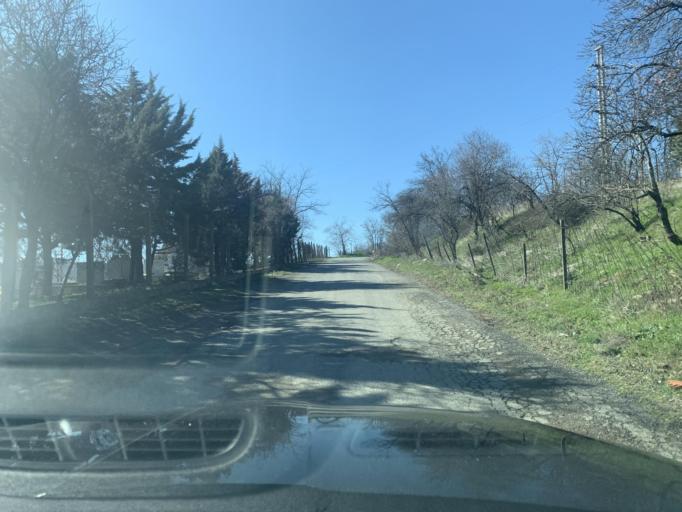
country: MK
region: Demir Kapija
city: Demir Kapija
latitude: 41.4092
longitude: 22.2339
